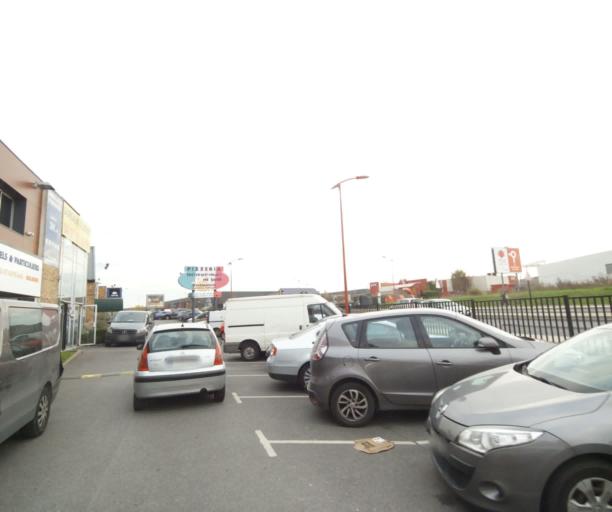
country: FR
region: Ile-de-France
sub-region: Departement du Val-d'Oise
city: Gonesse
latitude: 48.9825
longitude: 2.4425
